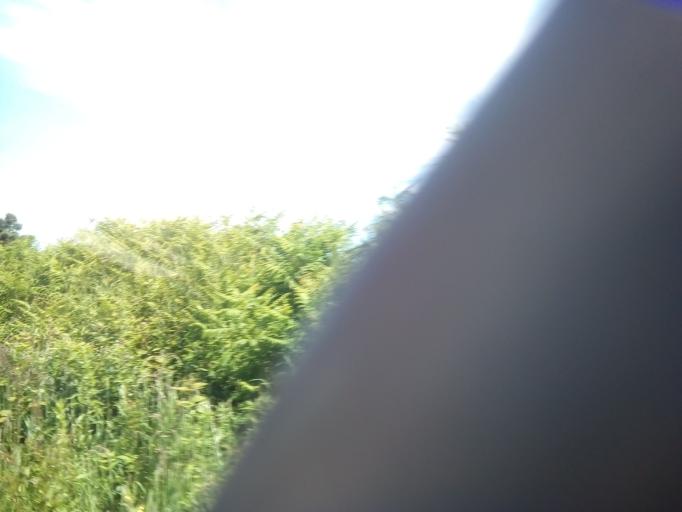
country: IE
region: Leinster
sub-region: Loch Garman
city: Loch Garman
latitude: 52.2418
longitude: -6.6027
